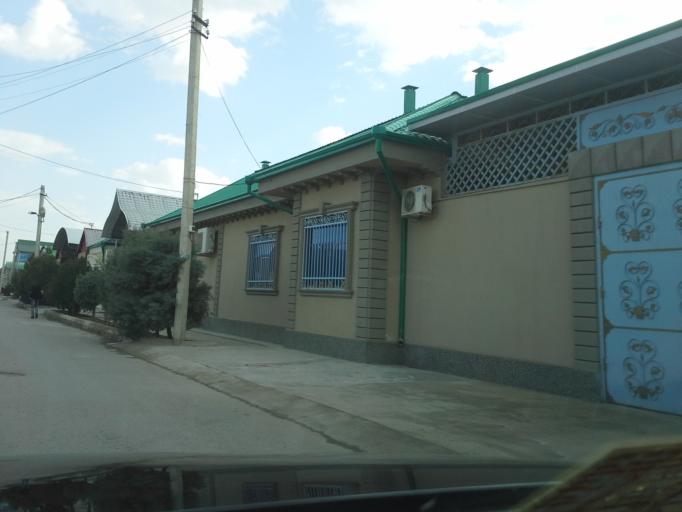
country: TM
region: Ahal
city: Ashgabat
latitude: 37.9949
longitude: 58.2940
